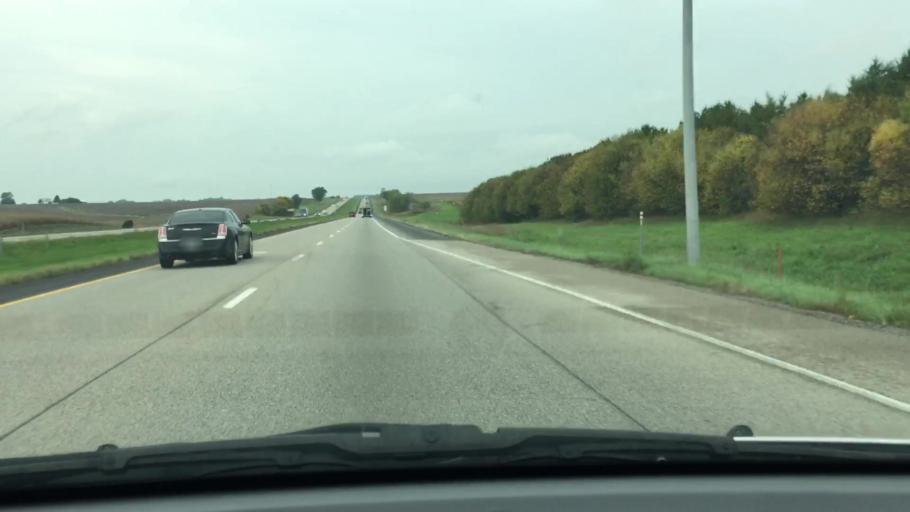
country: US
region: Iowa
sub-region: Cedar County
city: West Branch
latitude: 41.6640
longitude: -91.2549
